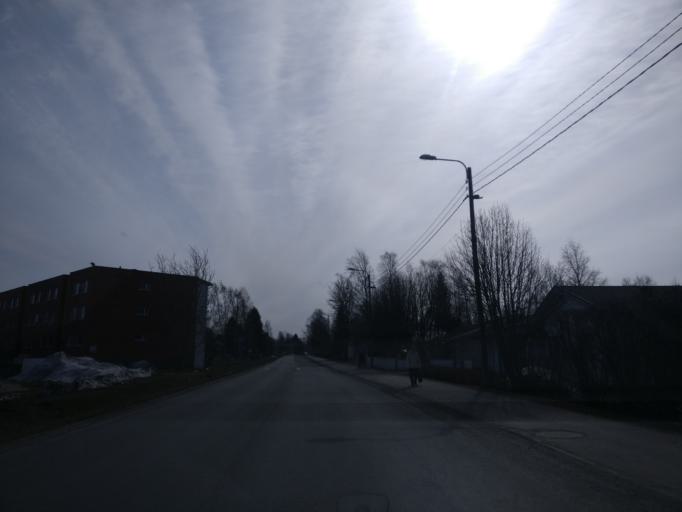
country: FI
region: Lapland
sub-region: Kemi-Tornio
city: Kemi
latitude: 65.7515
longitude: 24.5562
